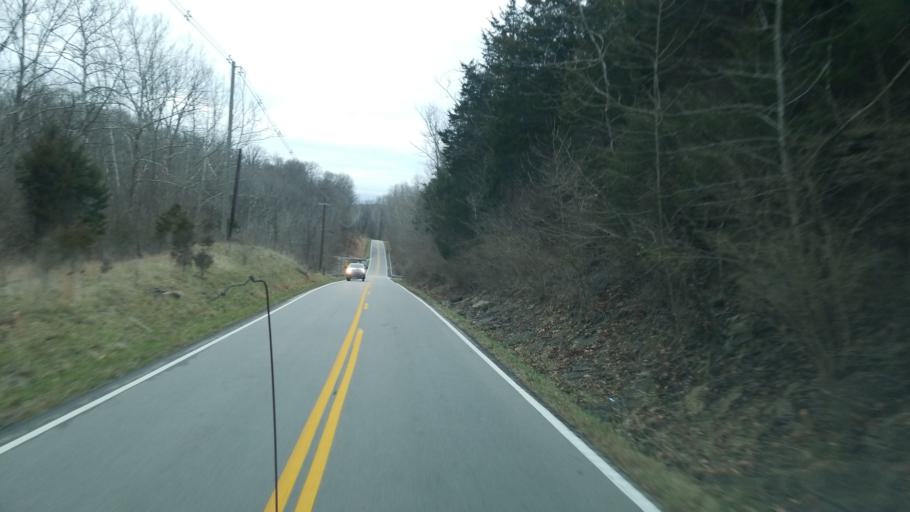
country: US
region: Ohio
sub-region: Clermont County
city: New Richmond
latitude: 38.8748
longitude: -84.2423
